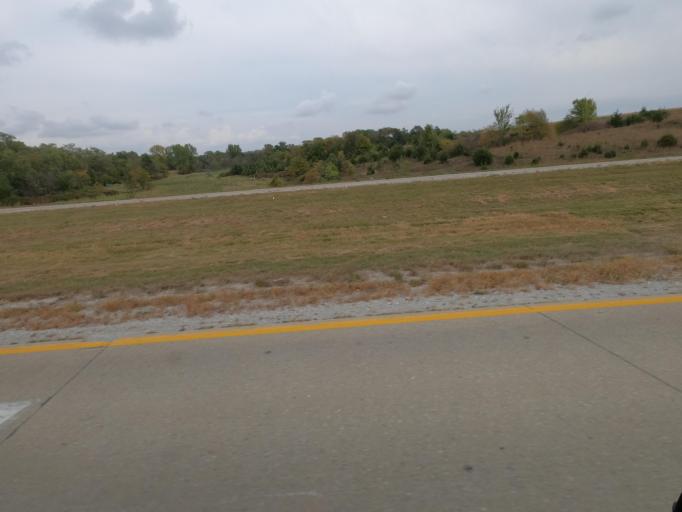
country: US
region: Iowa
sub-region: Jasper County
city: Monroe
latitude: 41.5142
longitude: -93.1274
